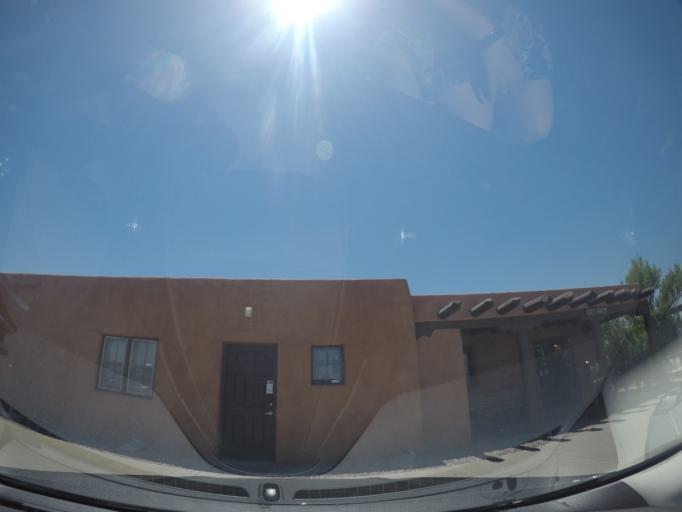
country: US
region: New Mexico
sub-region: Otero County
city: Holloman Air Force Base
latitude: 32.7798
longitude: -106.1726
